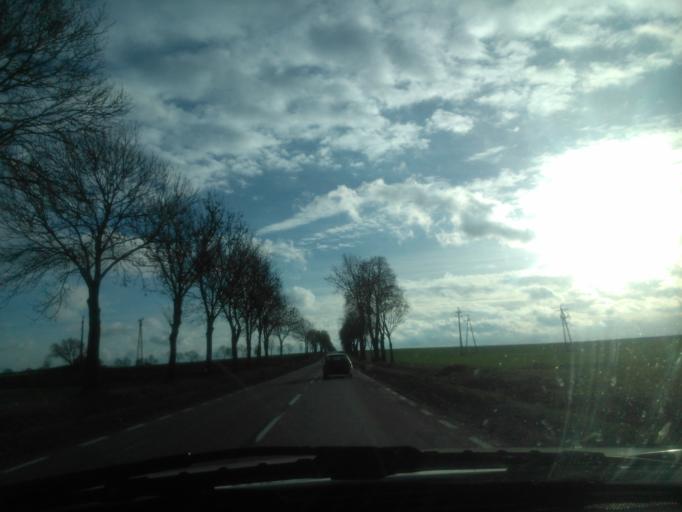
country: PL
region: Podlasie
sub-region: Powiat kolnenski
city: Kolno
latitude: 53.3980
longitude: 21.9438
